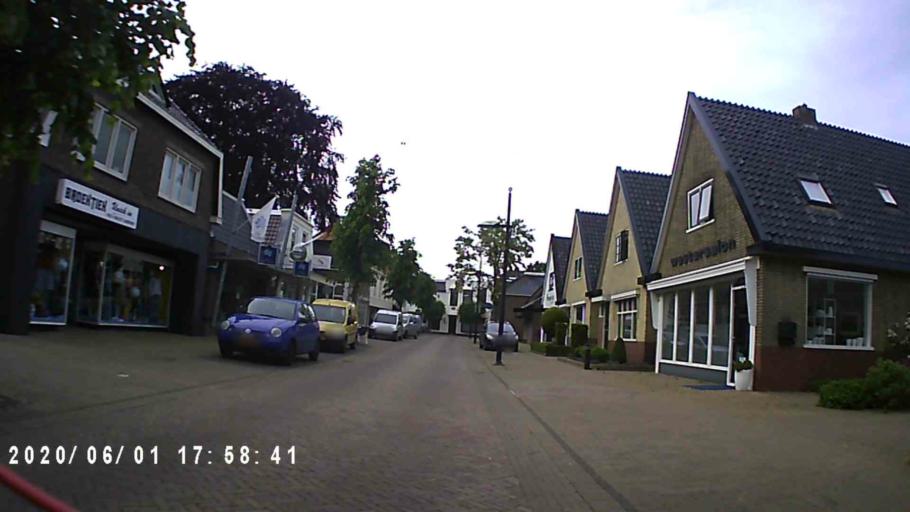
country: NL
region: Friesland
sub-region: Gemeente Tytsjerksteradiel
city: Burgum
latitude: 53.1919
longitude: 5.9905
